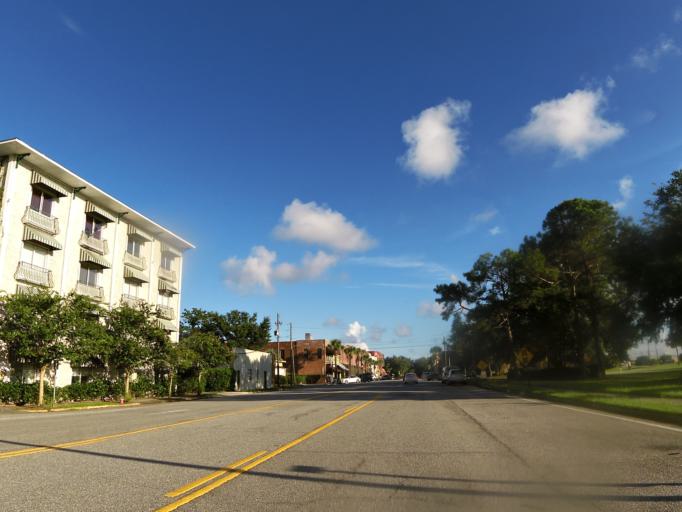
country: US
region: Georgia
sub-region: Glynn County
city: Brunswick
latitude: 31.1525
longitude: -81.4967
